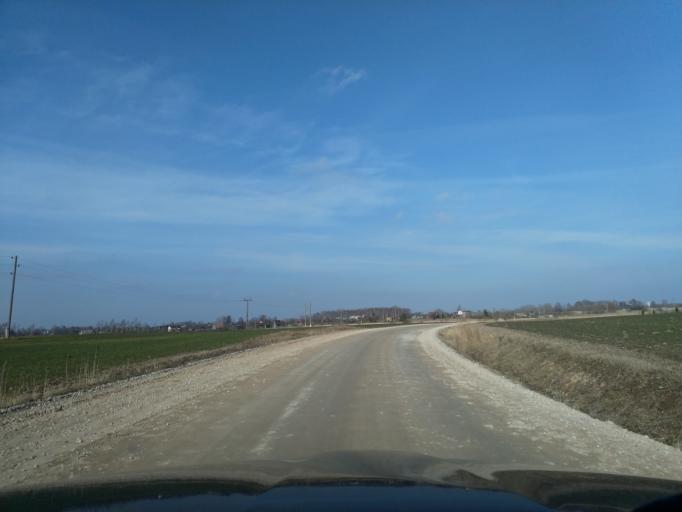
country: LV
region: Kuldigas Rajons
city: Kuldiga
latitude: 56.9436
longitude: 21.9754
